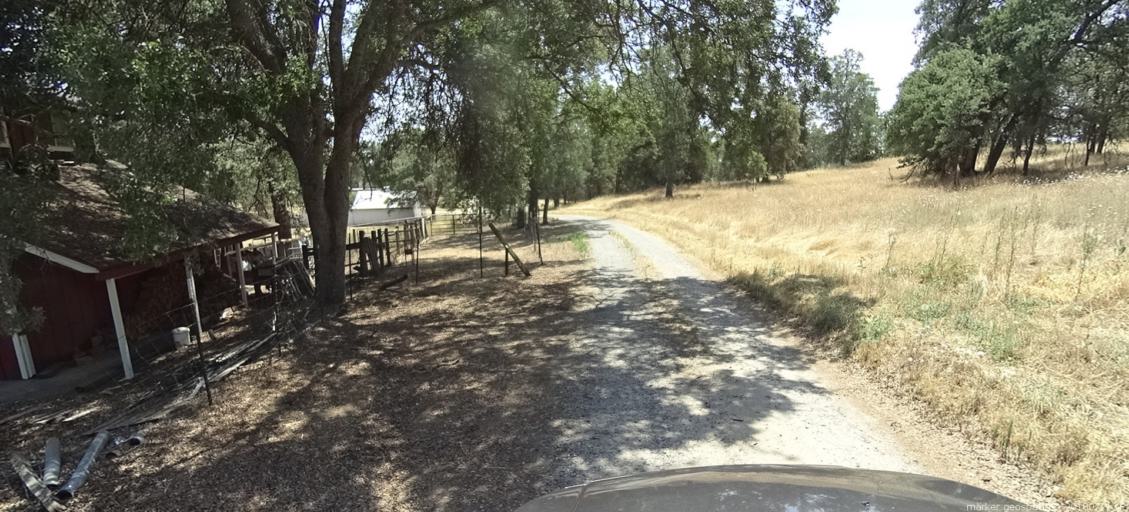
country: US
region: California
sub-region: Madera County
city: Oakhurst
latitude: 37.2219
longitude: -119.5467
